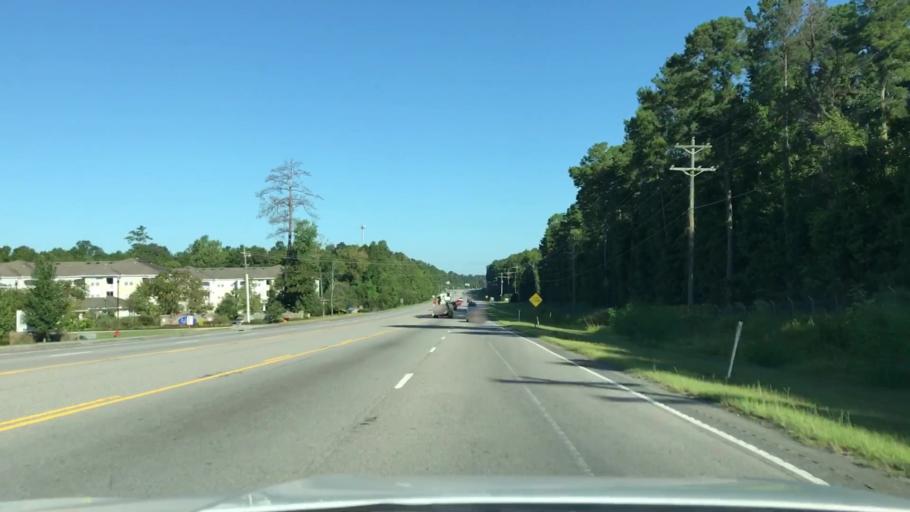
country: US
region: South Carolina
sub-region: Berkeley County
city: Sangaree
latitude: 33.0372
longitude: -80.0650
